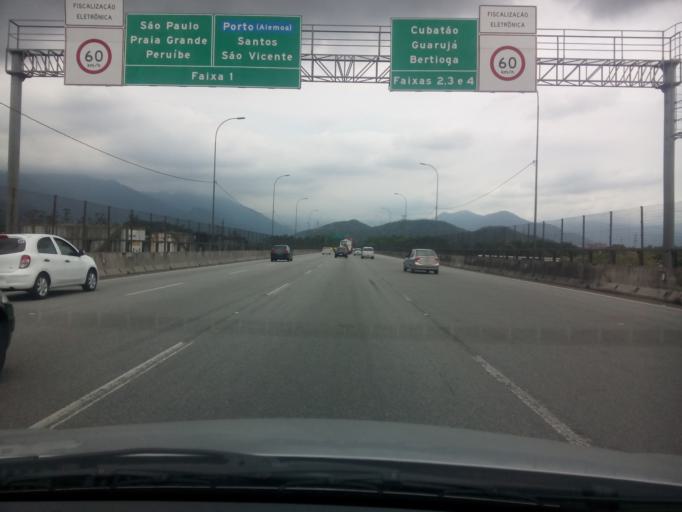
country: BR
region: Sao Paulo
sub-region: Cubatao
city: Cubatao
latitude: -23.8904
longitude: -46.4346
